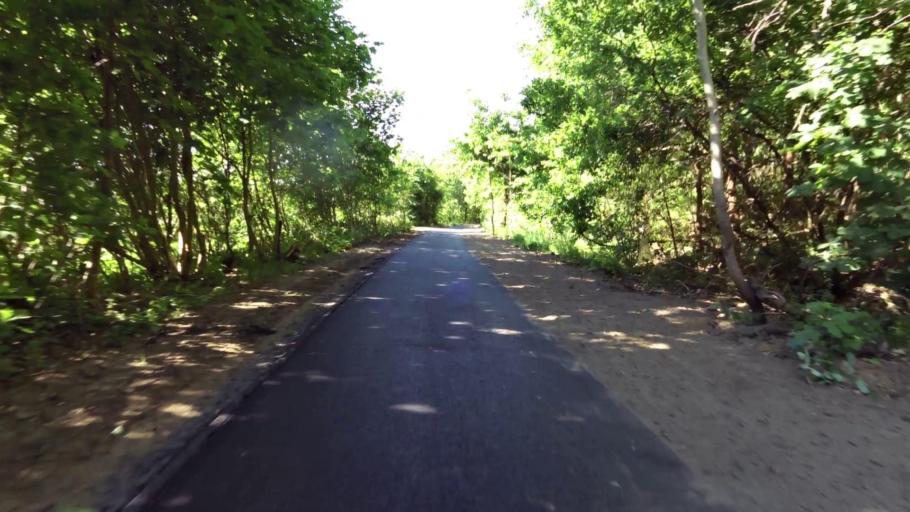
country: PL
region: West Pomeranian Voivodeship
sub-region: Powiat gryfinski
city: Banie
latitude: 53.1947
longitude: 14.6196
